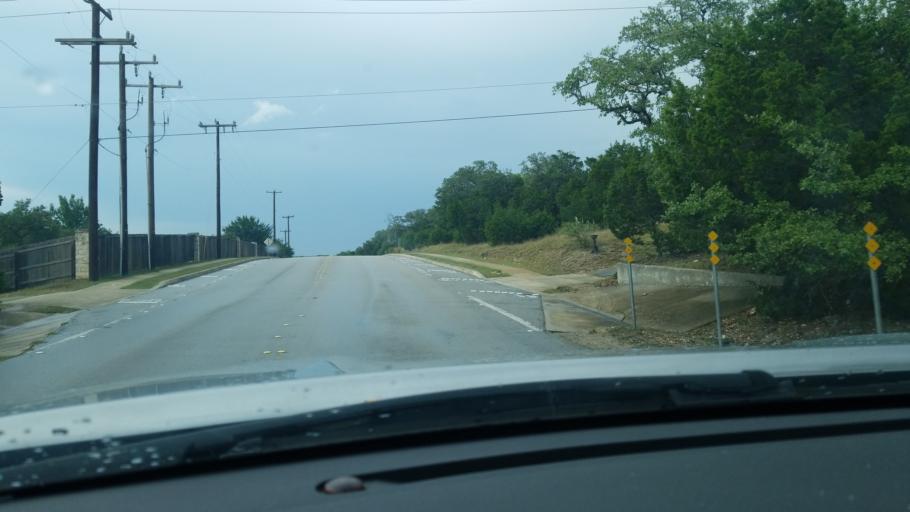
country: US
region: Texas
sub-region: Bexar County
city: Timberwood Park
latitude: 29.6864
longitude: -98.4792
